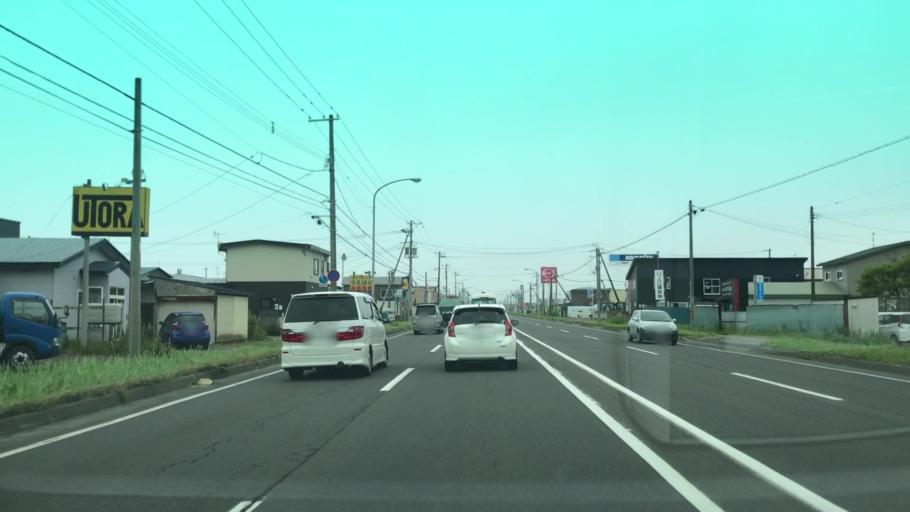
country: JP
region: Hokkaido
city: Muroran
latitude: 42.3748
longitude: 141.0676
